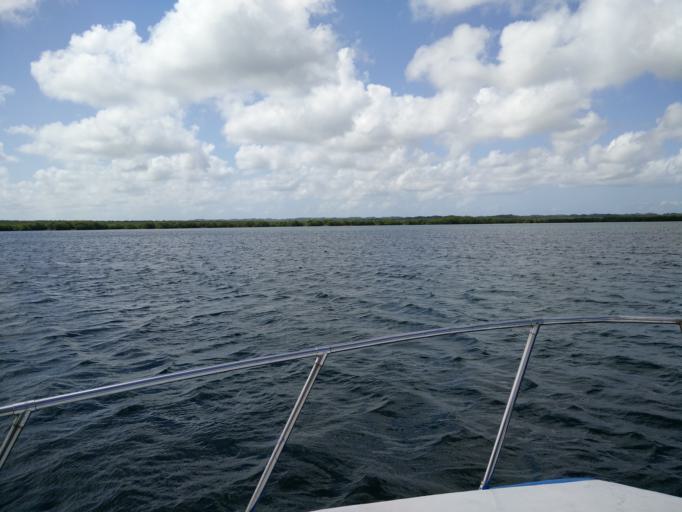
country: GP
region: Guadeloupe
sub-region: Guadeloupe
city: Petit-Canal
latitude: 16.3712
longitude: -61.5002
